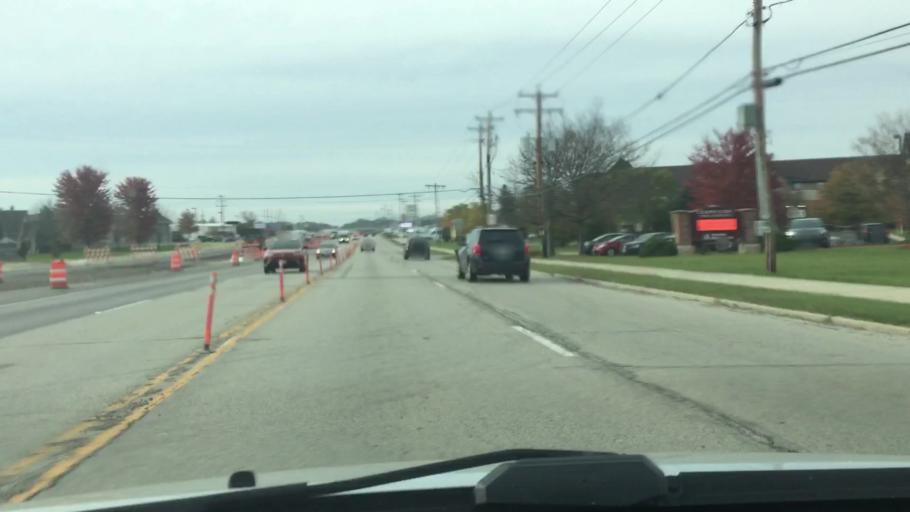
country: US
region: Wisconsin
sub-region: Milwaukee County
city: Hales Corners
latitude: 42.9327
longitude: -88.0486
